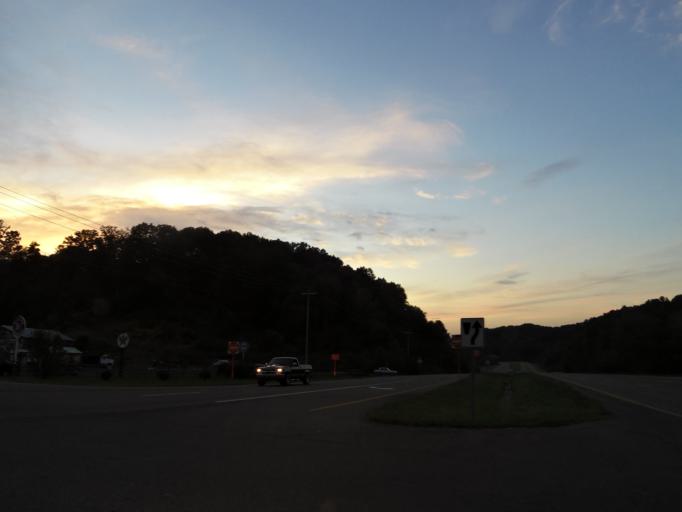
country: US
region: Tennessee
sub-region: Carter County
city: Elizabethton
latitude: 36.3733
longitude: -82.2148
